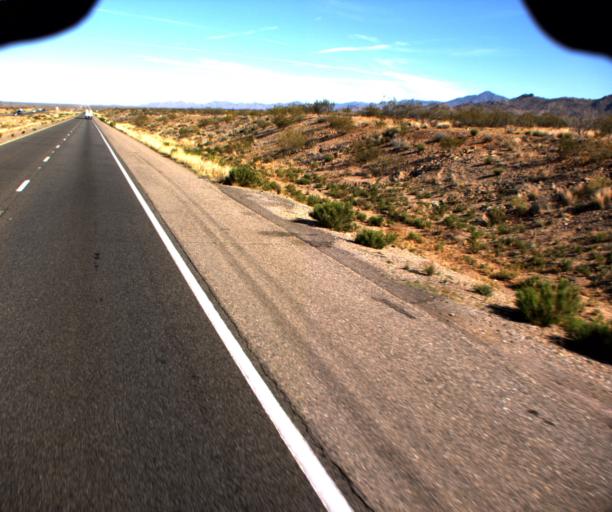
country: US
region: Arizona
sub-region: Mohave County
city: Golden Valley
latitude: 35.2518
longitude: -114.1540
